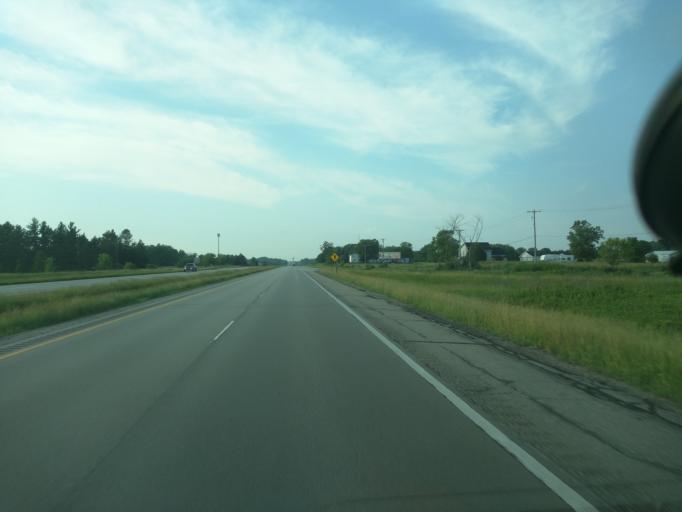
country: US
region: Michigan
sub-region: Ingham County
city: Mason
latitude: 42.5261
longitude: -84.4432
